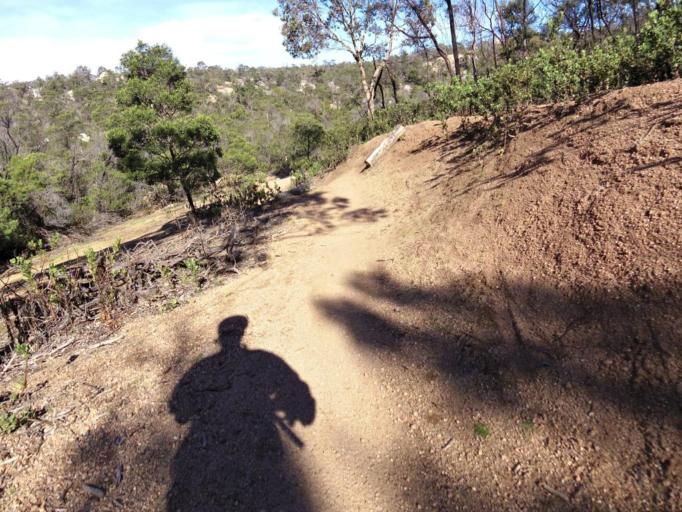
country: AU
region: Victoria
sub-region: Wyndham
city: Little River
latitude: -37.9271
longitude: 144.4344
